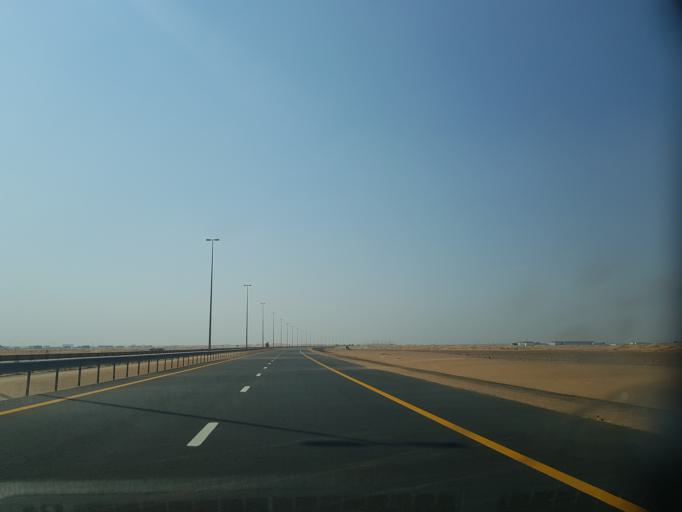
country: AE
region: Ash Shariqah
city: Sharjah
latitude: 25.2714
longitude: 55.6335
